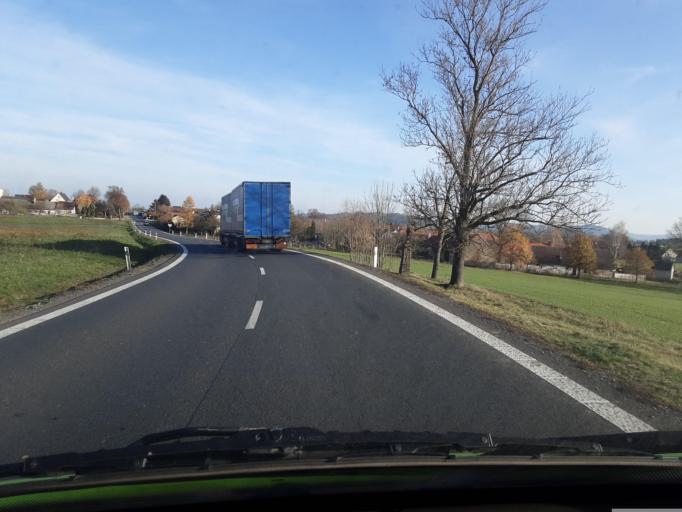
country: CZ
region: Plzensky
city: Horazd'ovice
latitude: 49.3250
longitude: 13.5912
